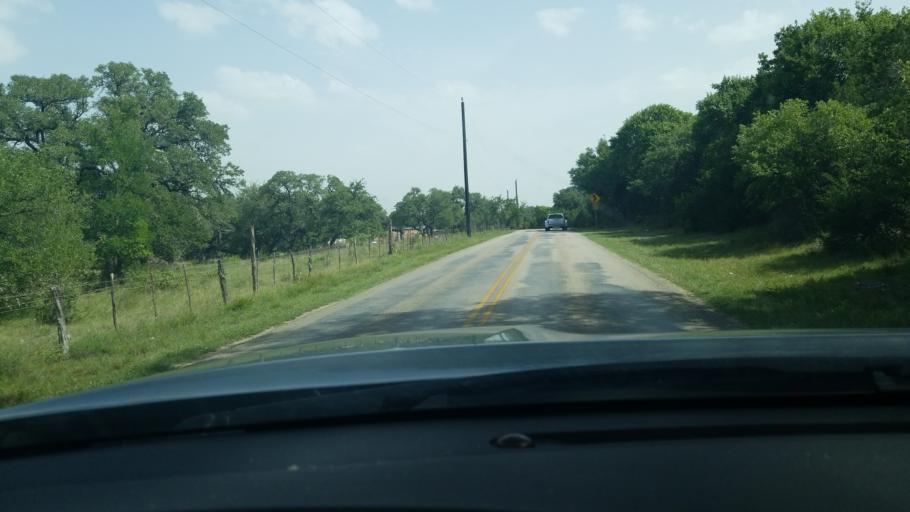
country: US
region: Texas
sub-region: Comal County
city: Bulverde
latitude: 29.7542
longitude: -98.4593
